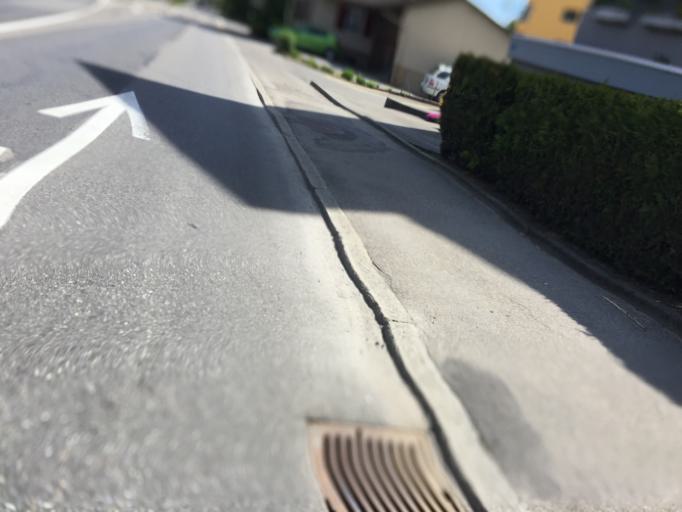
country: CH
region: Bern
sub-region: Bern-Mittelland District
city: Konolfingen
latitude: 46.8809
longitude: 7.6240
